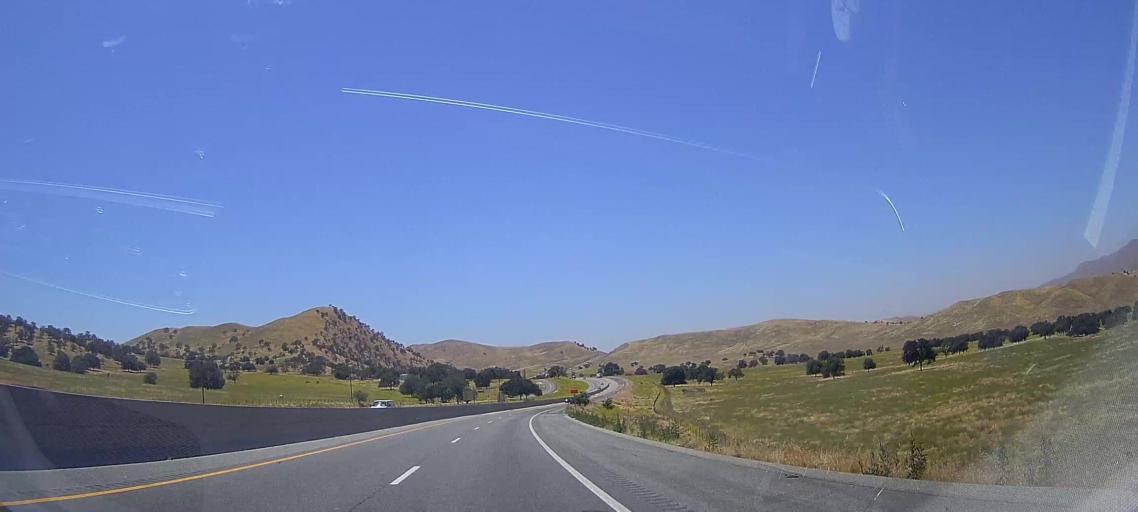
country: US
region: California
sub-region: Kern County
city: Bear Valley Springs
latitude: 35.2629
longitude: -118.6407
